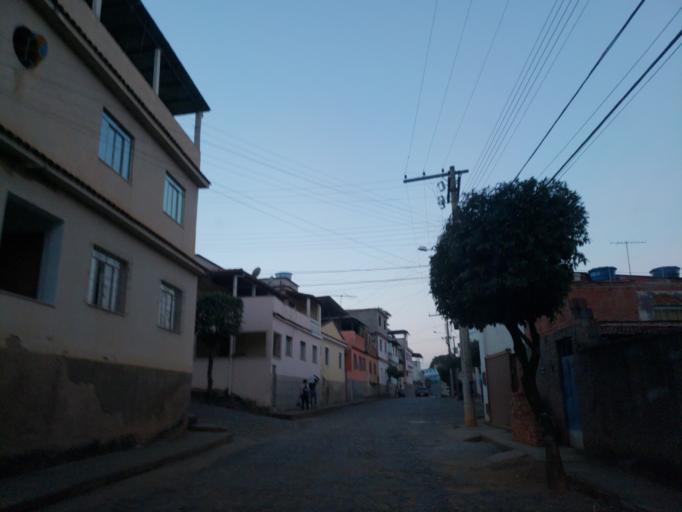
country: BR
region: Minas Gerais
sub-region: Sao Joao Nepomuceno
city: Sao Joao Nepomuceno
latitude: -21.5209
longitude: -43.0152
